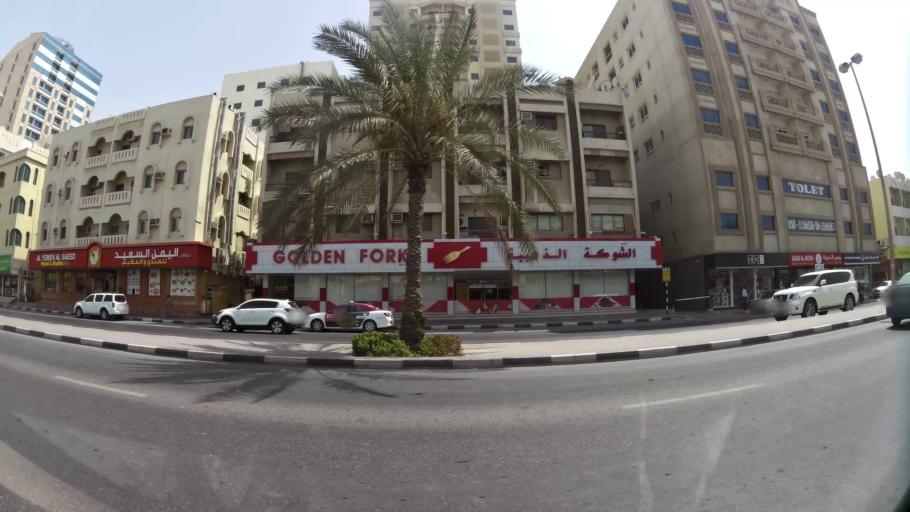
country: AE
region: Ash Shariqah
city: Sharjah
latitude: 25.3465
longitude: 55.4001
